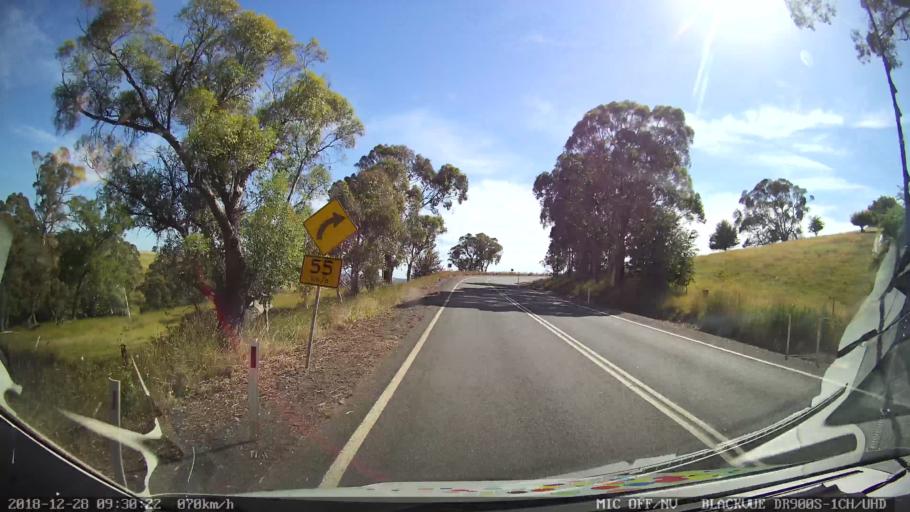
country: AU
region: New South Wales
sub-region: Upper Lachlan Shire
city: Crookwell
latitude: -34.4496
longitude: 149.4391
